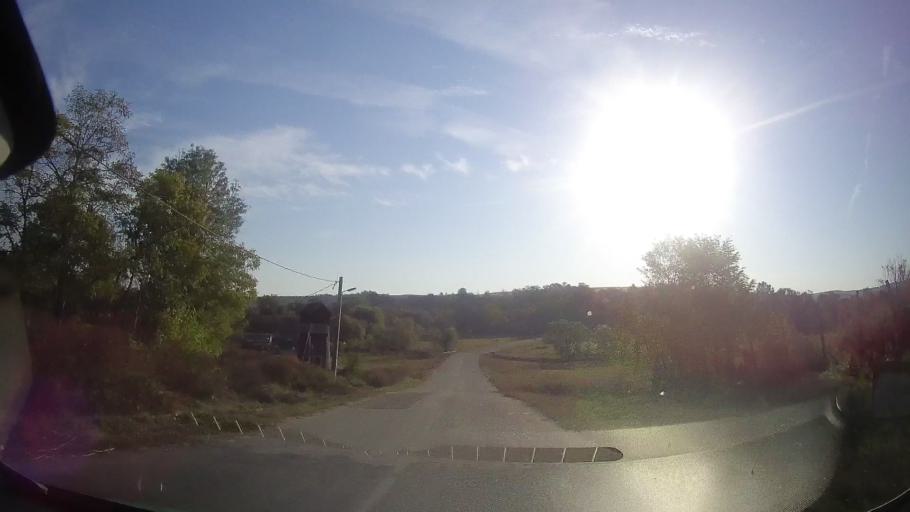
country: RO
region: Timis
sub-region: Comuna Bogda
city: Bogda
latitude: 45.9739
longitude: 21.5989
